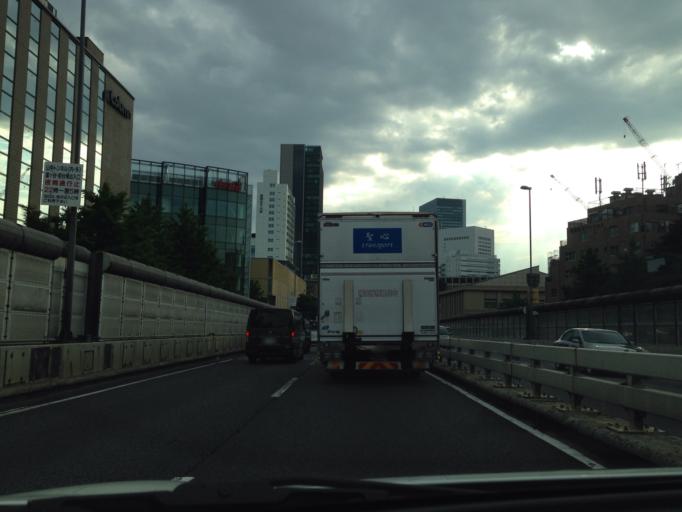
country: JP
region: Tokyo
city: Tokyo
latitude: 35.6589
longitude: 139.7136
